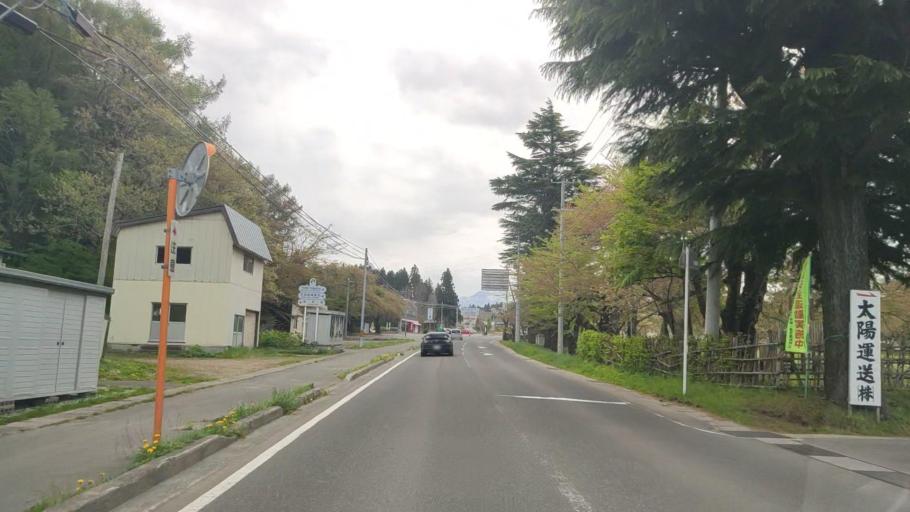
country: JP
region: Aomori
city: Aomori Shi
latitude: 40.7863
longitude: 140.7890
